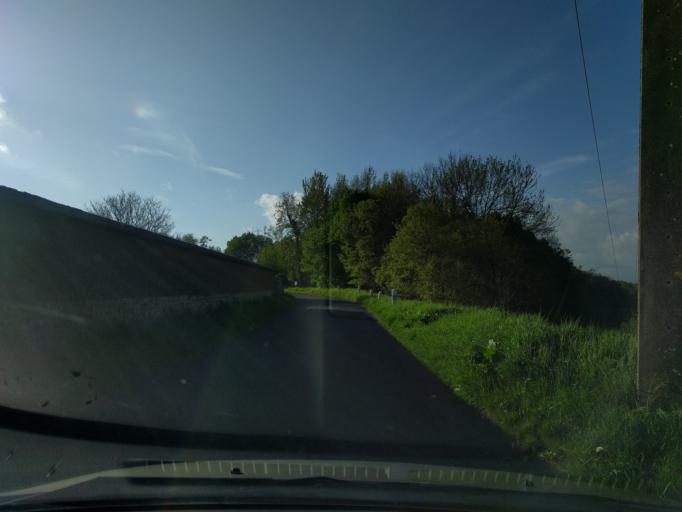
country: FR
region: Haute-Normandie
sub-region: Departement de l'Eure
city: Damville
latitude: 48.8908
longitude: 1.0746
